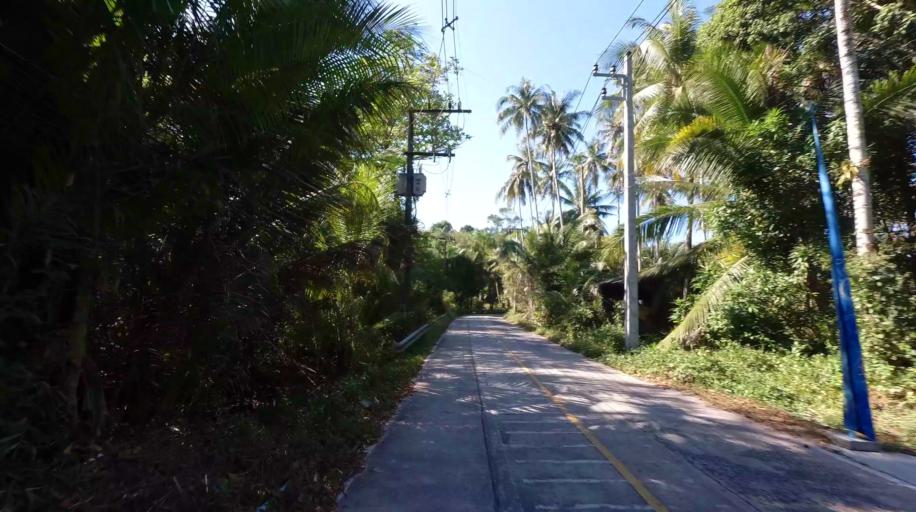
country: TH
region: Trat
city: Ko Kut
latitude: 11.6210
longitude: 102.5462
